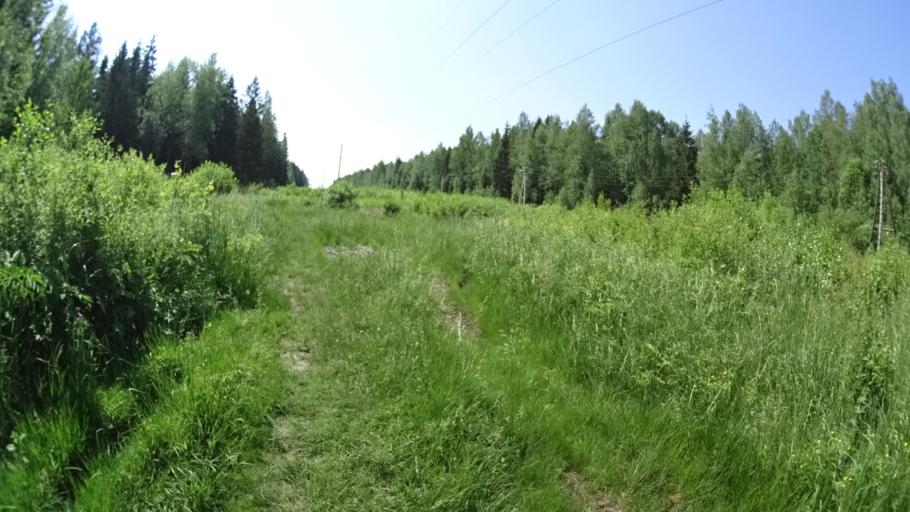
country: RU
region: Moskovskaya
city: Lesnoy
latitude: 56.0809
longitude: 37.9587
